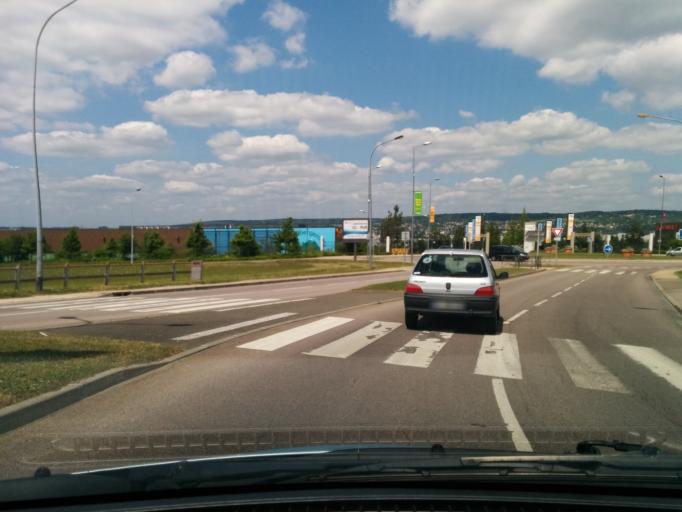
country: FR
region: Ile-de-France
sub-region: Departement des Yvelines
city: Aubergenville
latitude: 48.9619
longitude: 1.8581
